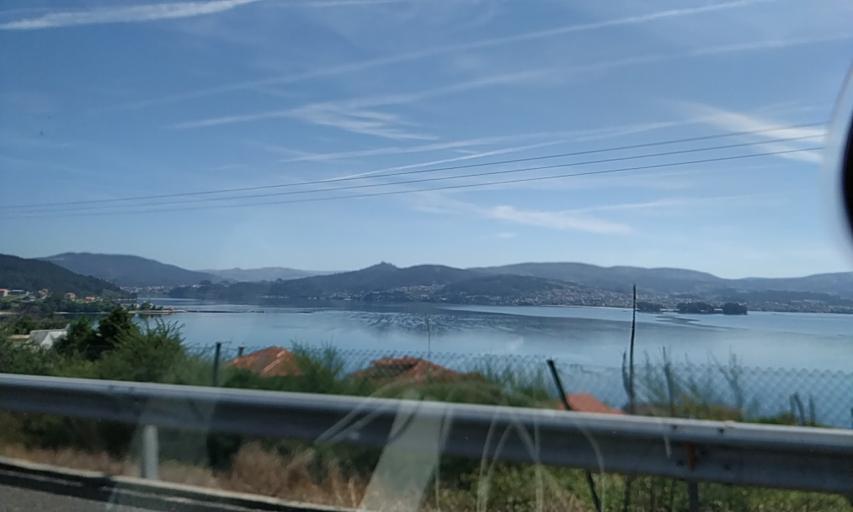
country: ES
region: Galicia
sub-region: Provincia de Pontevedra
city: Redondela
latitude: 42.3127
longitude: -8.6648
